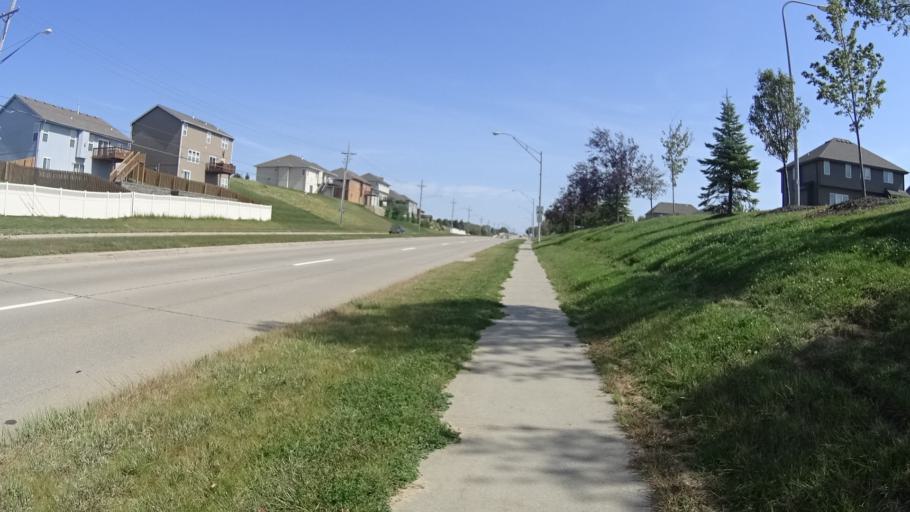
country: US
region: Nebraska
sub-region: Sarpy County
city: Papillion
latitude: 41.1762
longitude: -96.0763
